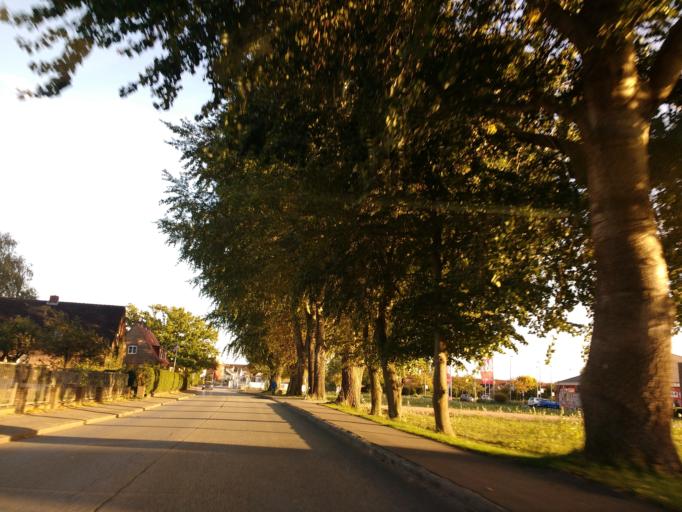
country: DE
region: Schleswig-Holstein
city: Kellenhusen
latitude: 54.1933
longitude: 11.0547
